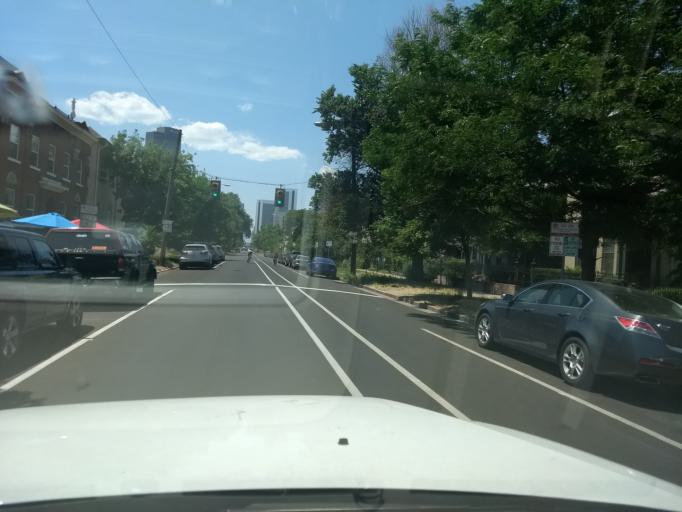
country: US
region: Colorado
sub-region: Denver County
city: Denver
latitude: 39.7555
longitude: -104.9822
